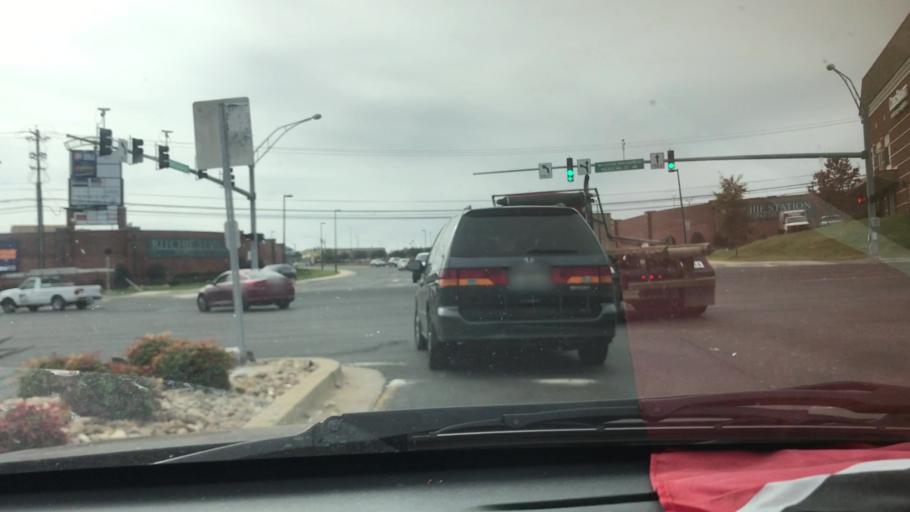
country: US
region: Maryland
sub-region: Prince George's County
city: Largo
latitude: 38.8696
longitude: -76.8504
